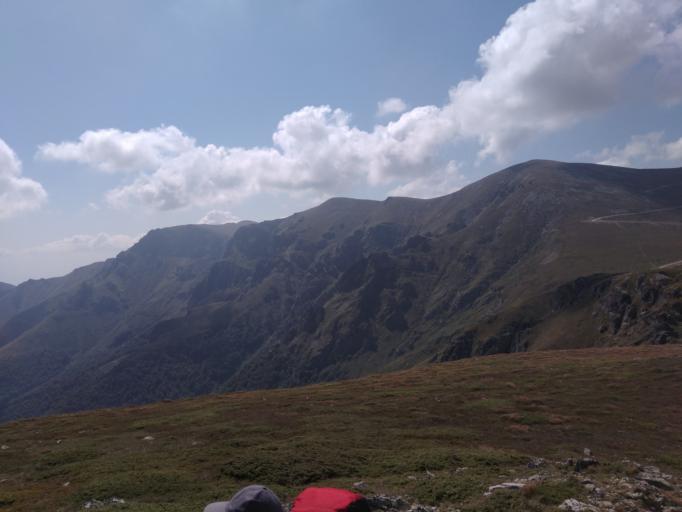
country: BG
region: Plovdiv
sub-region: Obshtina Karlovo
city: Kalofer
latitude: 42.7484
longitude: 25.0711
